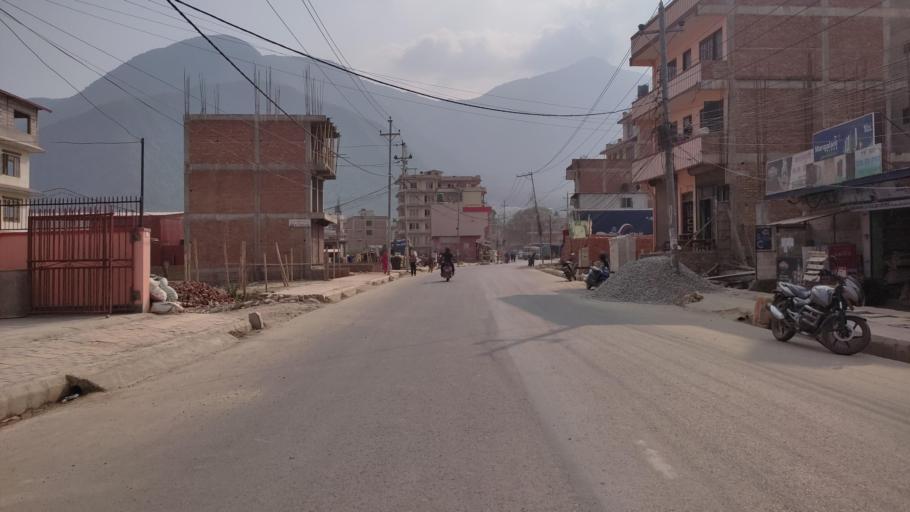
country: NP
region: Central Region
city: Kirtipur
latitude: 27.6681
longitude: 85.2680
